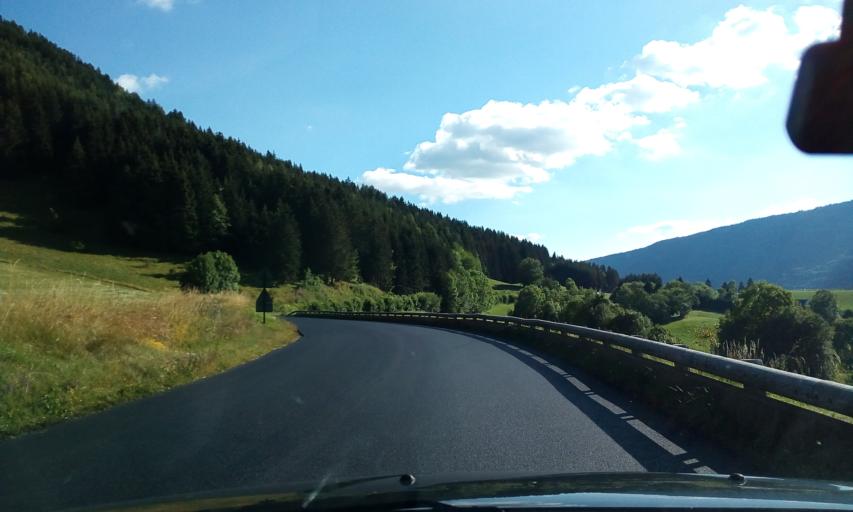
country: FR
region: Rhone-Alpes
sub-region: Departement de l'Isere
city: Seyssins
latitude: 45.1637
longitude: 5.6261
